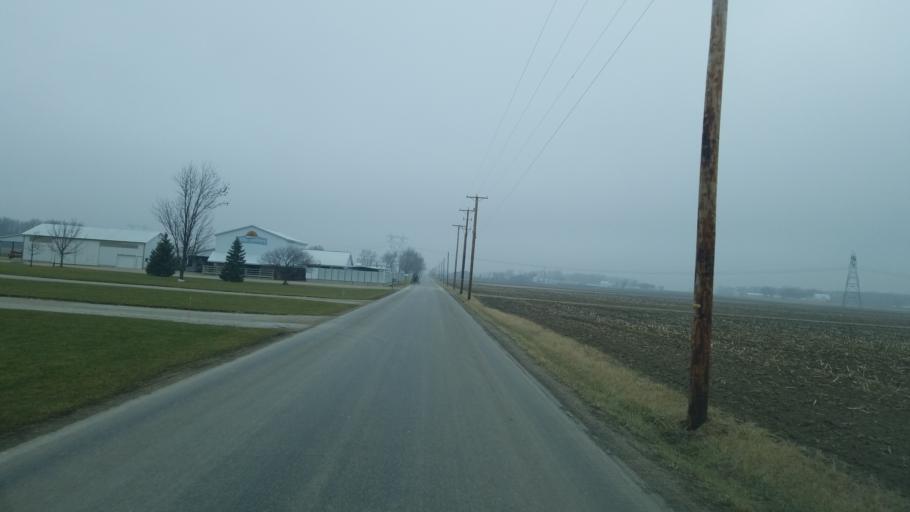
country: US
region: Indiana
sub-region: Adams County
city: Berne
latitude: 40.7050
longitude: -84.9753
